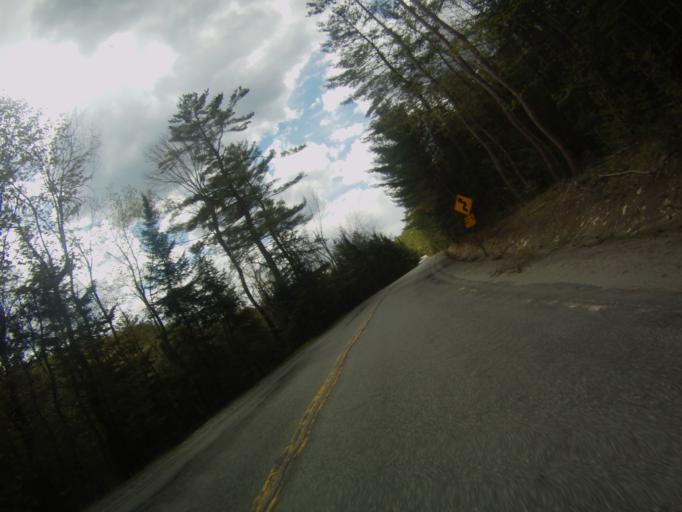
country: US
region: New York
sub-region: Essex County
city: Mineville
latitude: 44.0756
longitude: -73.6514
